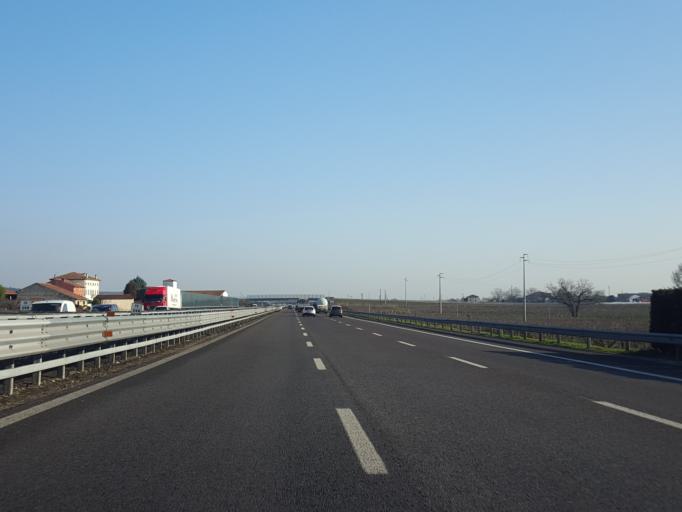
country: IT
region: Veneto
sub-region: Provincia di Verona
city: Caldiero
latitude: 45.4138
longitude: 11.2049
